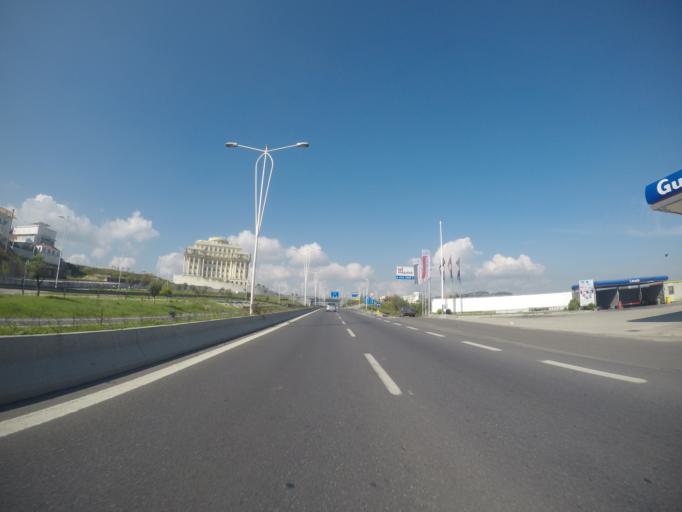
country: AL
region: Tirane
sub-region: Rrethi i Tiranes
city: Kashar
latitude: 41.3658
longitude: 19.7069
